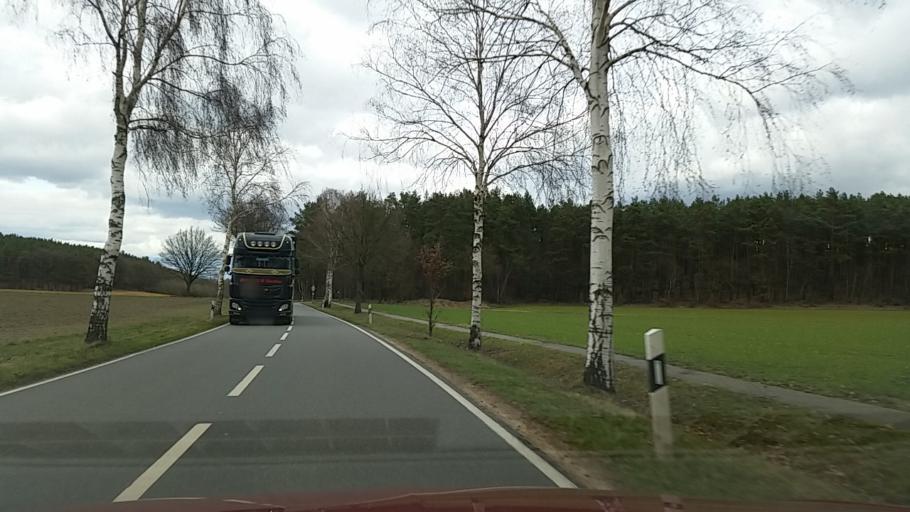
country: DE
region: Lower Saxony
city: Karwitz
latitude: 53.1192
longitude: 10.9522
